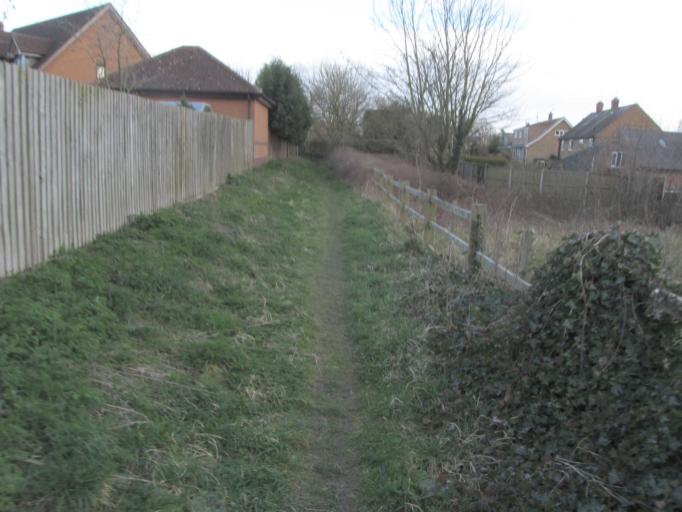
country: GB
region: England
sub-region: Nottinghamshire
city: East Leake
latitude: 52.8147
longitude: -1.1464
